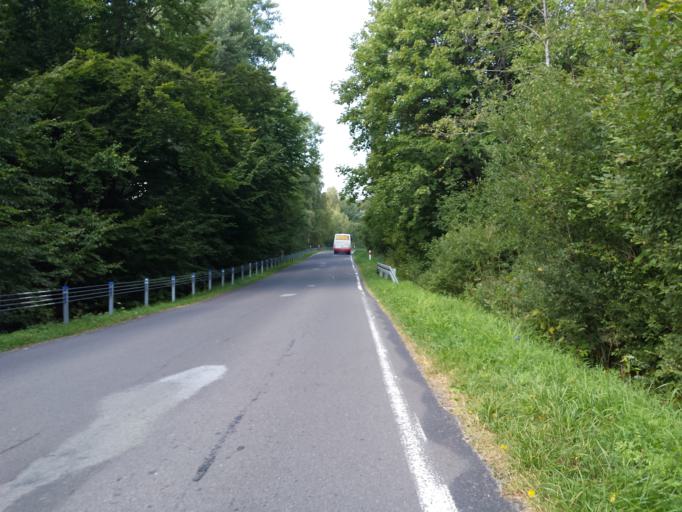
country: PL
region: Subcarpathian Voivodeship
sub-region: Powiat bieszczadzki
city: Lutowiska
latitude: 49.1223
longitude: 22.6005
